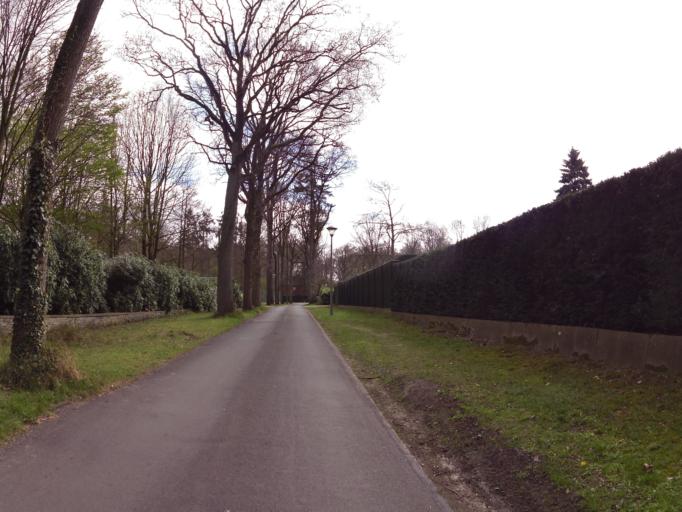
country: BE
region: Flanders
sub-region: Provincie West-Vlaanderen
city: Jabbeke
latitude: 51.1862
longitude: 3.1313
